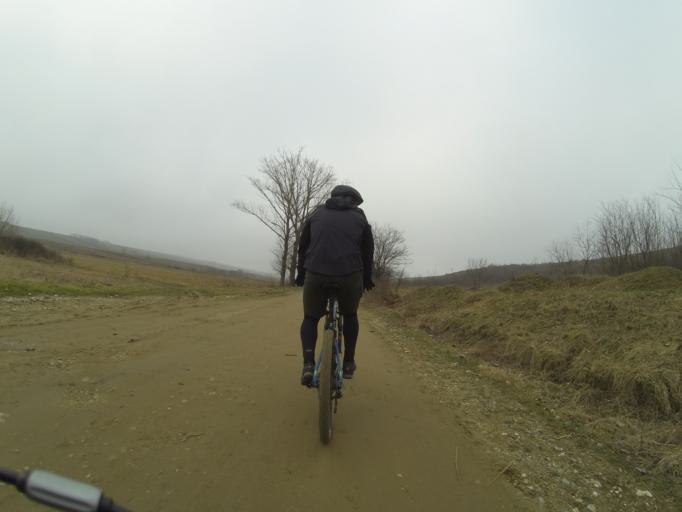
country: RO
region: Mehedinti
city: Padina Mica
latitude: 44.4872
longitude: 23.0214
